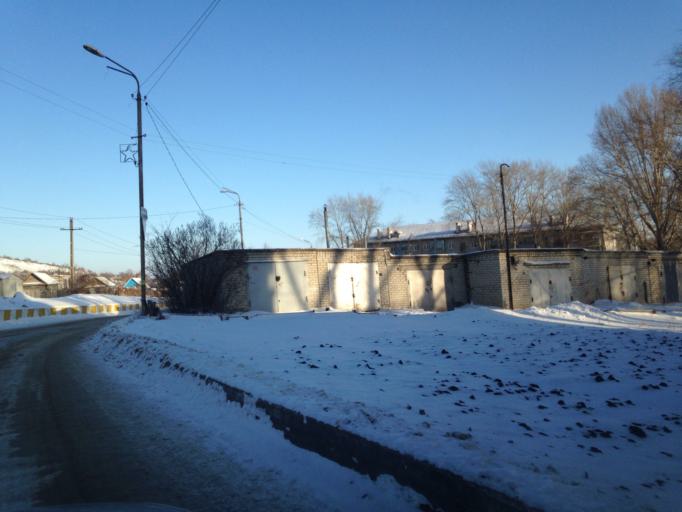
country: RU
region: Ulyanovsk
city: Novoul'yanovsk
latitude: 54.1528
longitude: 48.3785
